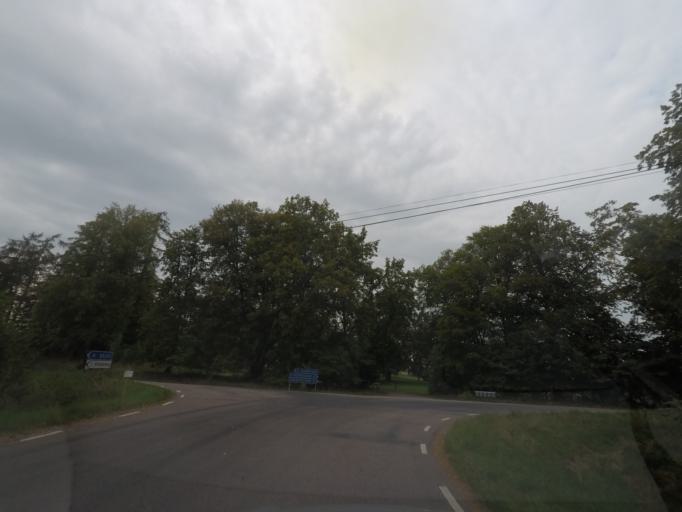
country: SE
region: Vaestmanland
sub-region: Hallstahammars Kommun
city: Kolback
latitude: 59.5233
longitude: 16.1908
